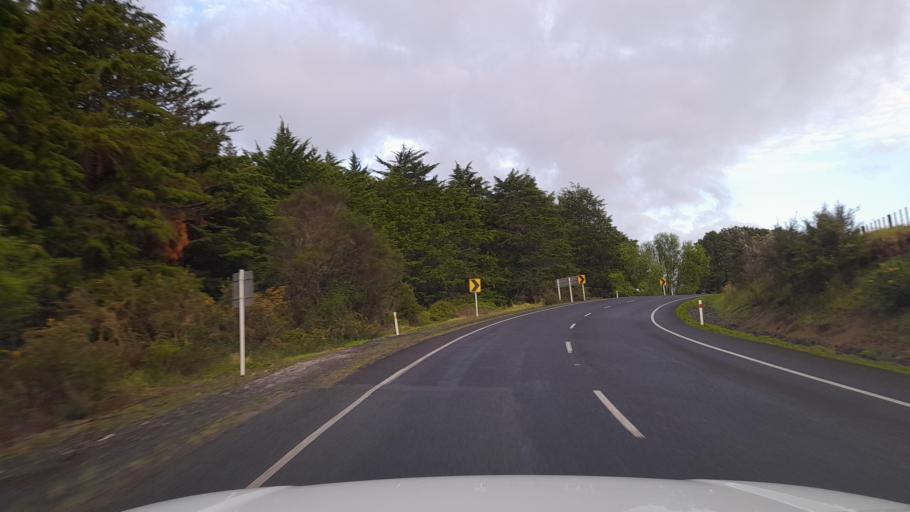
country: NZ
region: Northland
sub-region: Kaipara District
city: Dargaville
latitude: -35.6960
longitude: 173.9060
